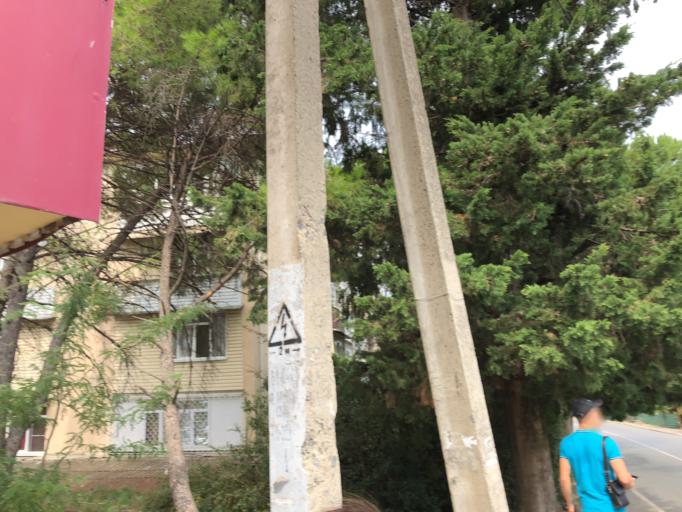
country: RU
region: Krasnodarskiy
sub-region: Sochi City
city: Sochi
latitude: 43.5912
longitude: 39.7402
